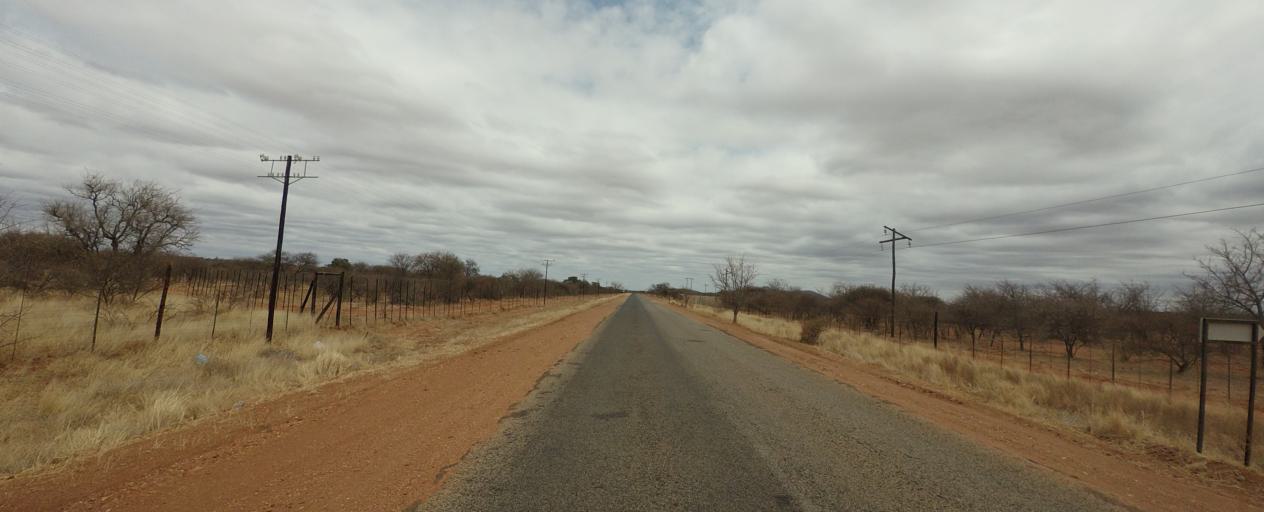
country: BW
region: Central
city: Mathathane
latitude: -22.6766
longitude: 29.0943
